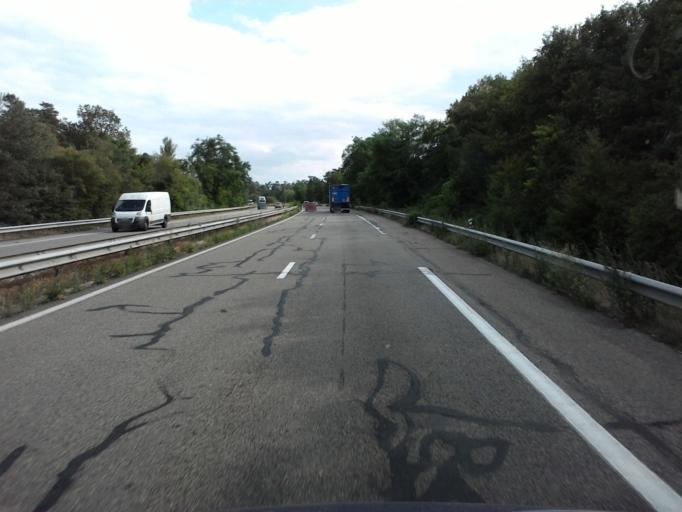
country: FR
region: Lorraine
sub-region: Departement des Vosges
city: Charmes
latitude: 48.3974
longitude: 6.2324
